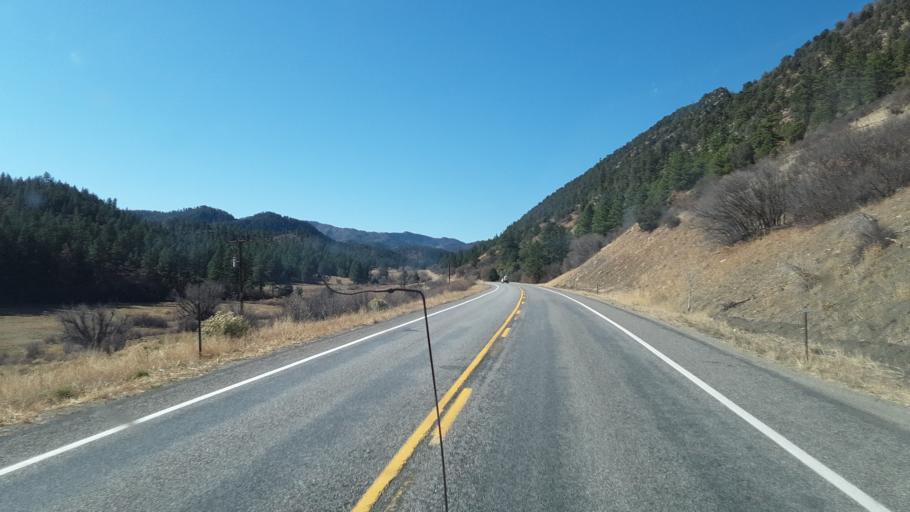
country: US
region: Colorado
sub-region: La Plata County
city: Bayfield
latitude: 37.2291
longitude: -107.3595
